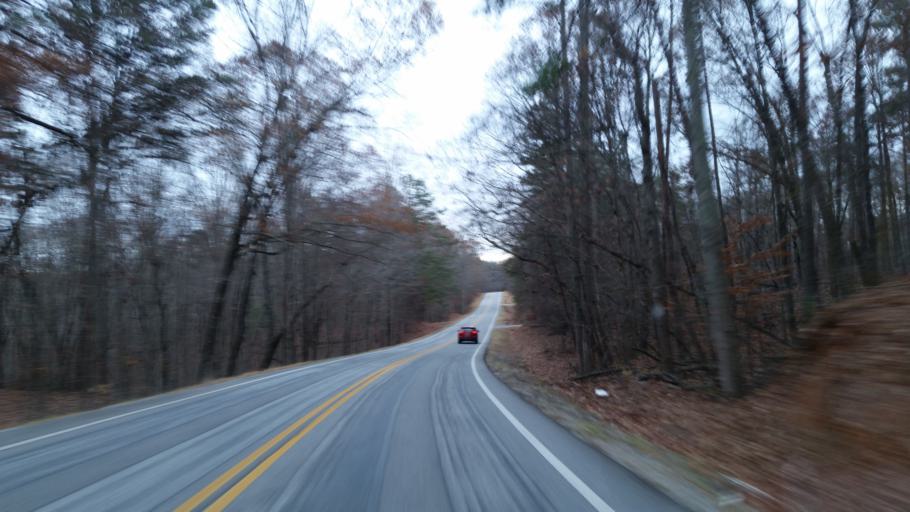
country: US
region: Georgia
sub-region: Dawson County
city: Dawsonville
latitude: 34.4306
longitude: -84.0551
